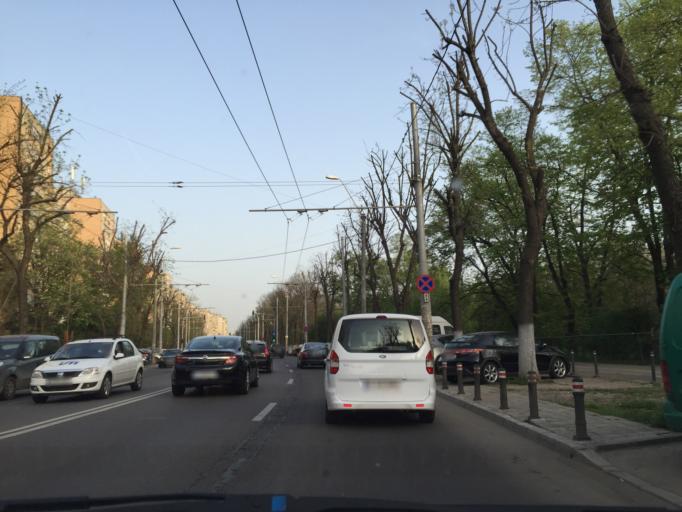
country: RO
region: Bucuresti
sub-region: Municipiul Bucuresti
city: Bucuresti
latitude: 44.4123
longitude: 26.1062
